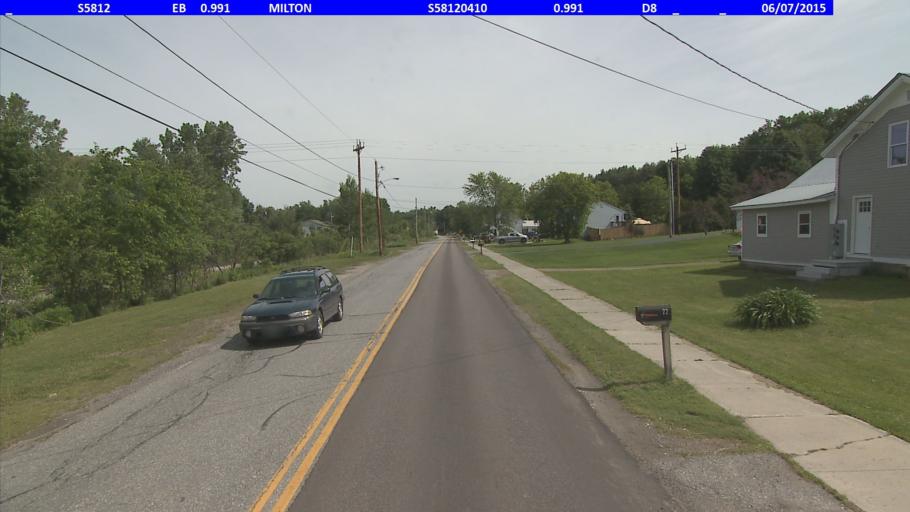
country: US
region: Vermont
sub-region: Chittenden County
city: Milton
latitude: 44.6329
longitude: -73.1065
